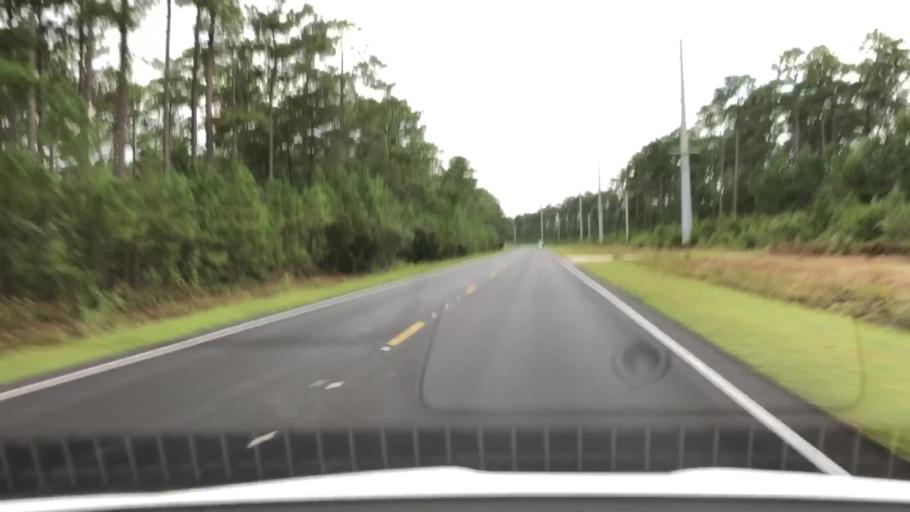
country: US
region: North Carolina
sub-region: Onslow County
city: Swansboro
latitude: 34.7840
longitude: -77.1146
